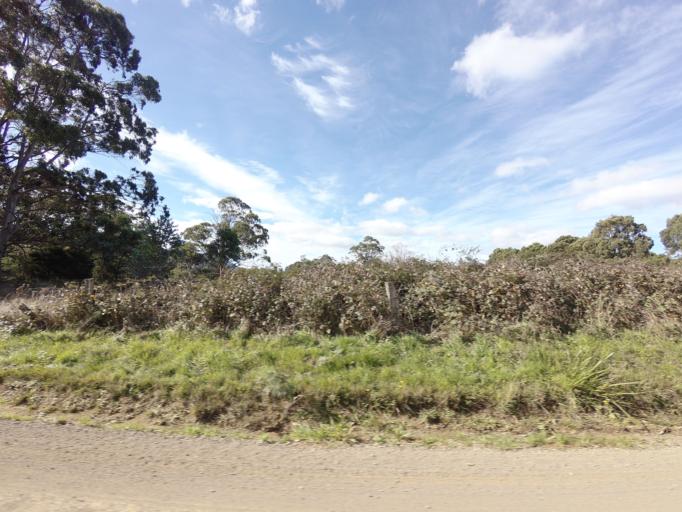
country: AU
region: Tasmania
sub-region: Clarence
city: Sandford
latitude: -43.1535
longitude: 147.7634
